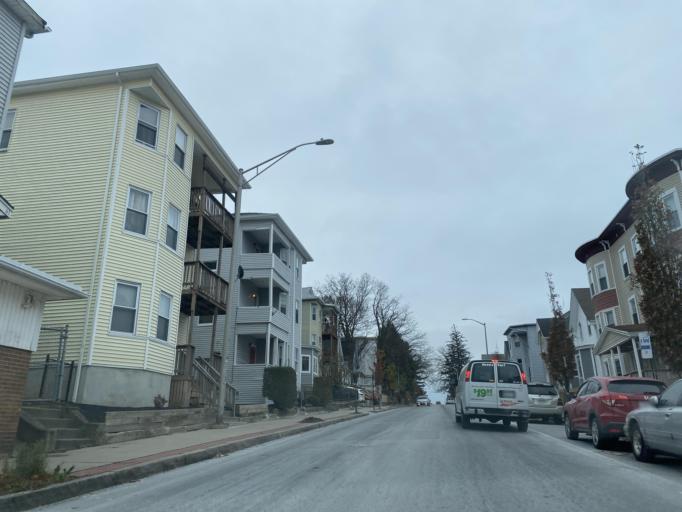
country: US
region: Massachusetts
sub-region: Worcester County
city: Worcester
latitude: 42.2546
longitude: -71.7928
